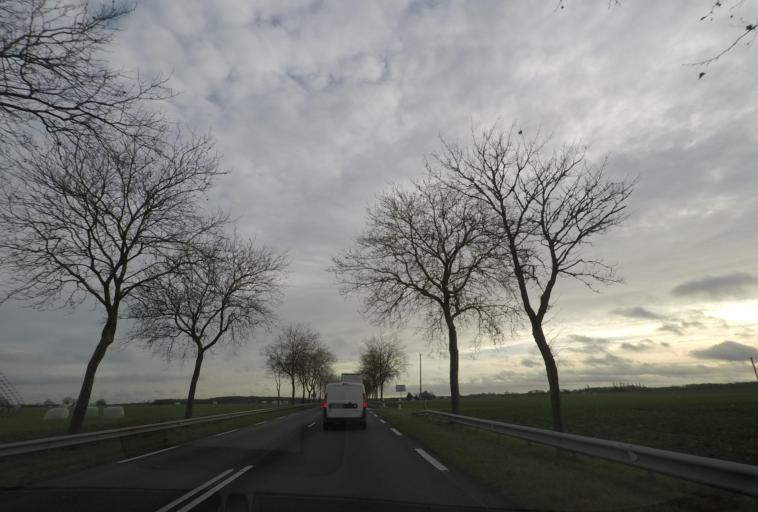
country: FR
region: Centre
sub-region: Departement du Loir-et-Cher
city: Sarge-sur-Braye
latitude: 47.9045
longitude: 0.8929
